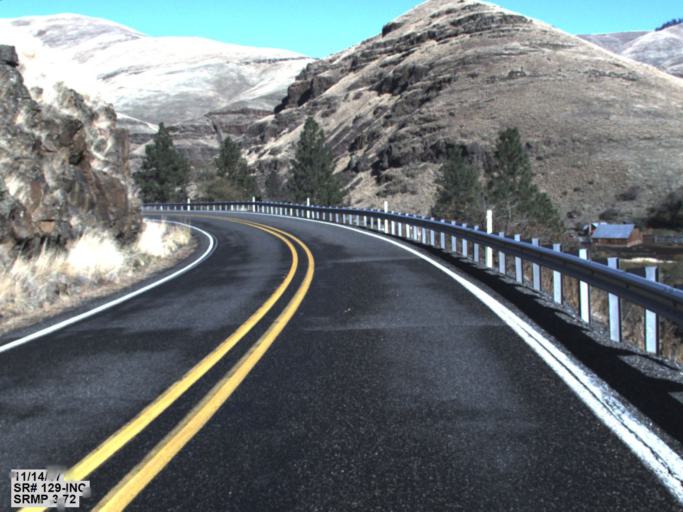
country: US
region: Washington
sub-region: Asotin County
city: Asotin
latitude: 46.0330
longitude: -117.2551
